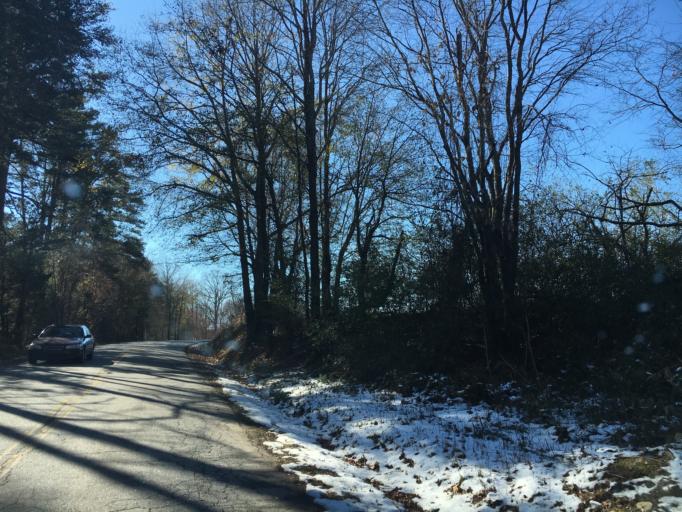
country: US
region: South Carolina
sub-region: Greenville County
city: Taylors
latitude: 34.9310
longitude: -82.2759
